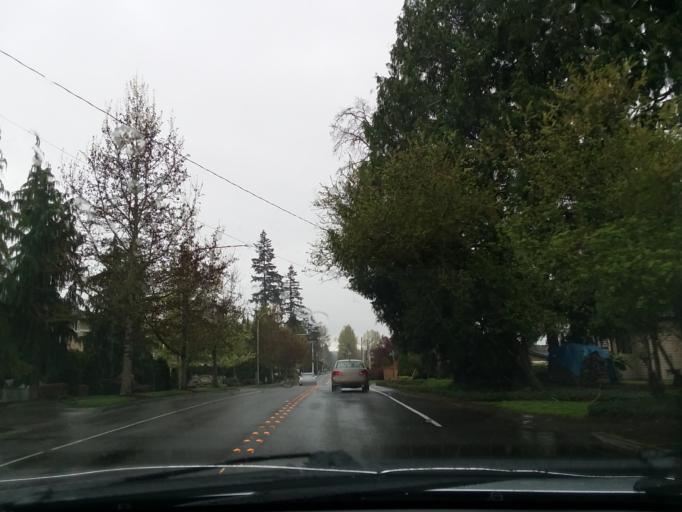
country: US
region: Washington
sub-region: King County
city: East Renton Highlands
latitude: 47.4876
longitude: -122.1484
